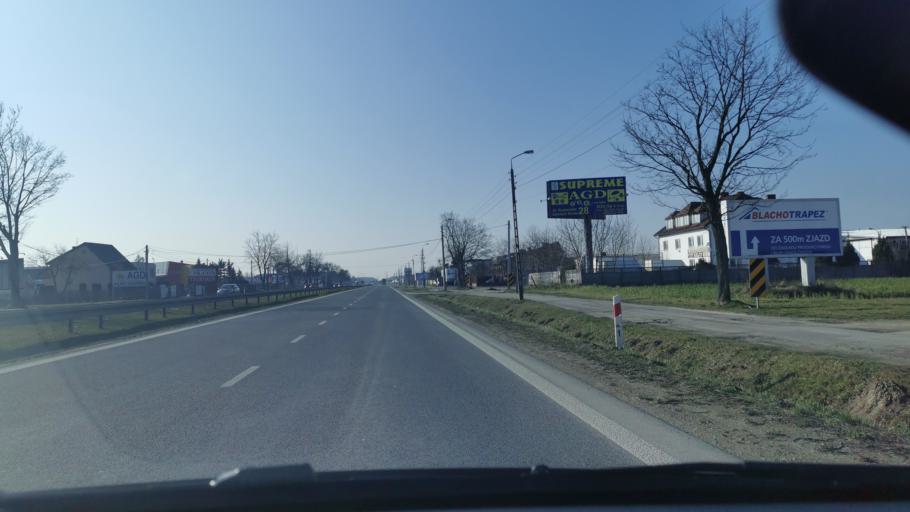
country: PL
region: Masovian Voivodeship
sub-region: Powiat pruszkowski
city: Nowe Grocholice
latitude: 52.1207
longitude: 20.8933
